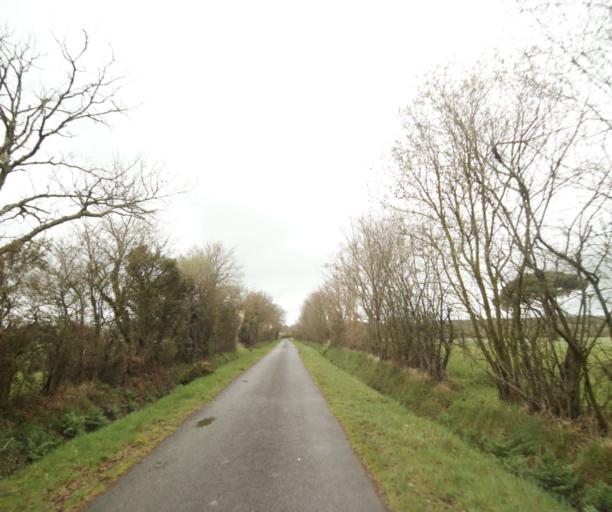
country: FR
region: Pays de la Loire
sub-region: Departement de la Loire-Atlantique
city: Quilly
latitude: 47.4580
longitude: -1.9009
